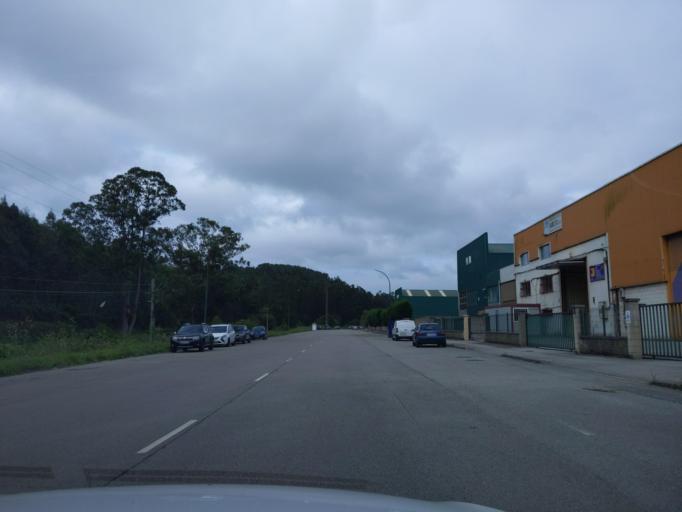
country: ES
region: Asturias
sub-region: Province of Asturias
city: Aviles
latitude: 43.6010
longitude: -5.9077
